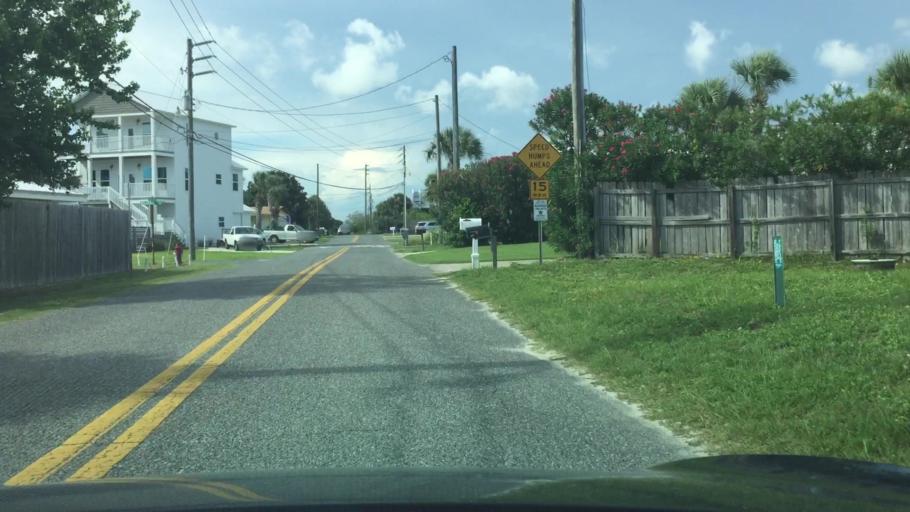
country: US
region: Florida
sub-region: Bay County
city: Laguna Beach
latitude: 30.2554
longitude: -85.9580
